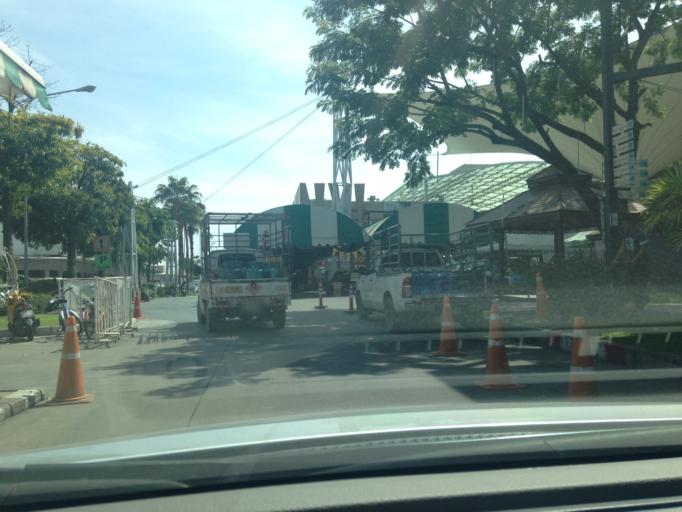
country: TH
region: Bangkok
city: Lat Krabang
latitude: 13.7205
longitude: 100.7275
